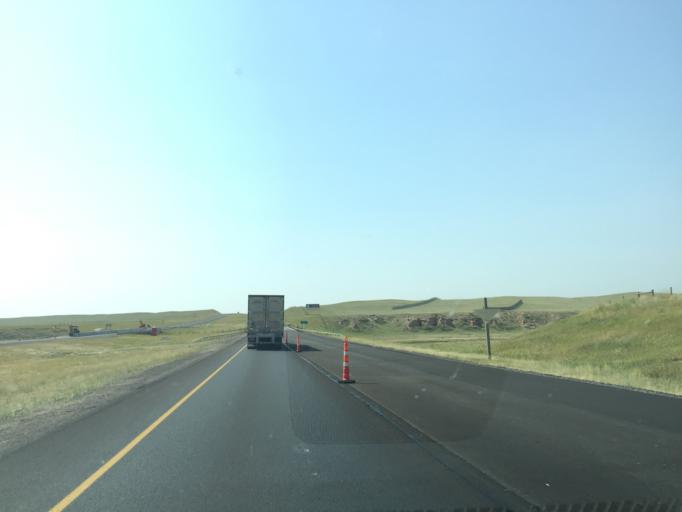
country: US
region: Wyoming
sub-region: Laramie County
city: Ranchettes
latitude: 41.3261
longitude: -104.8626
